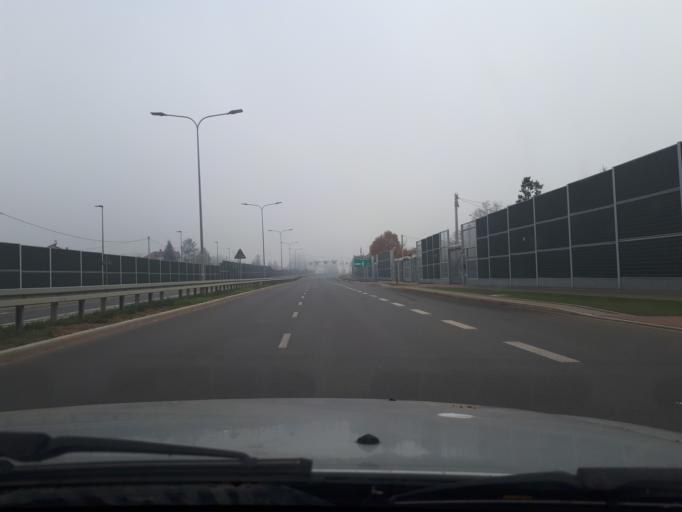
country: PL
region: Lesser Poland Voivodeship
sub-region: Powiat wielicki
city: Niepolomice
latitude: 50.0800
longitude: 20.1816
